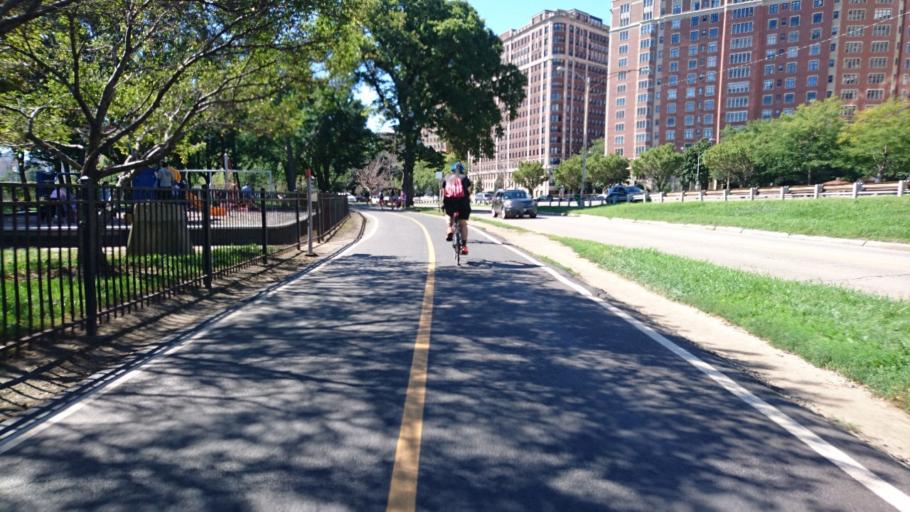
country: US
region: Illinois
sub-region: Cook County
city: Evanston
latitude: 41.9536
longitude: -87.6440
